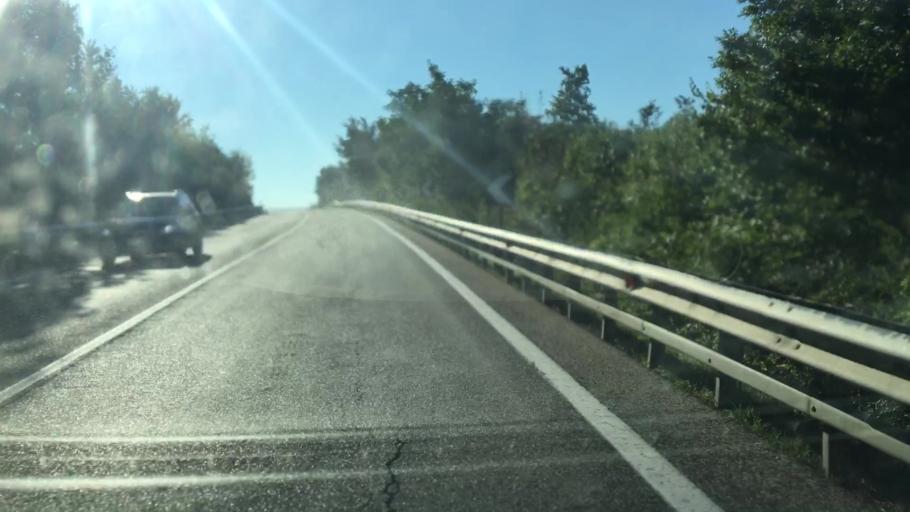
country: IT
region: Molise
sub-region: Provincia di Campobasso
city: Vinchiaturo
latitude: 41.4537
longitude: 14.5836
